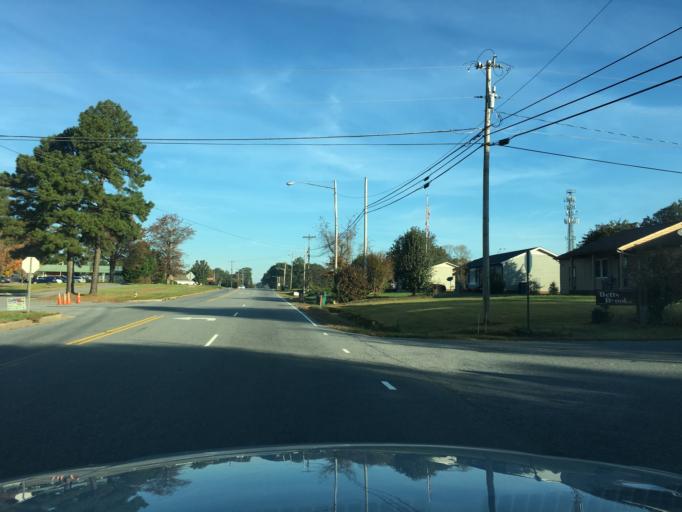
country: US
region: North Carolina
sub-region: Catawba County
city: Newton
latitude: 35.6373
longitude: -81.2678
